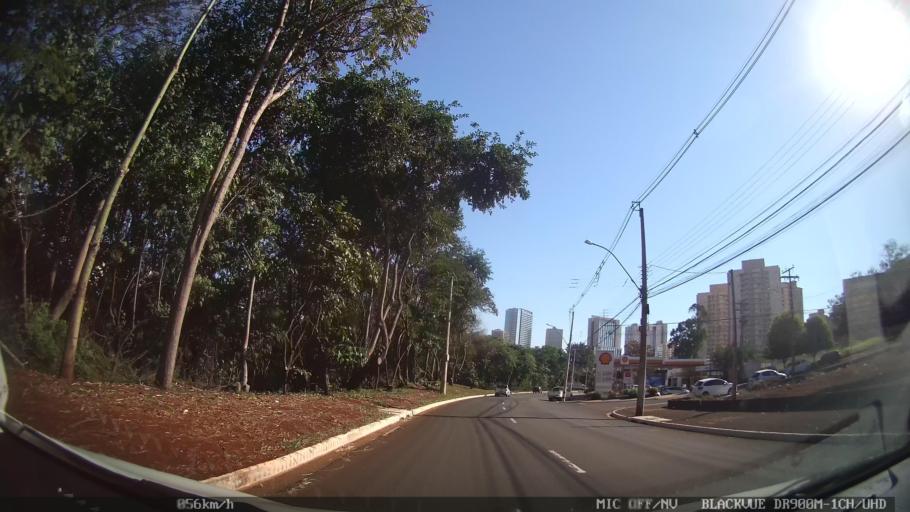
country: BR
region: Sao Paulo
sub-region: Ribeirao Preto
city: Ribeirao Preto
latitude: -21.2156
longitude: -47.7948
